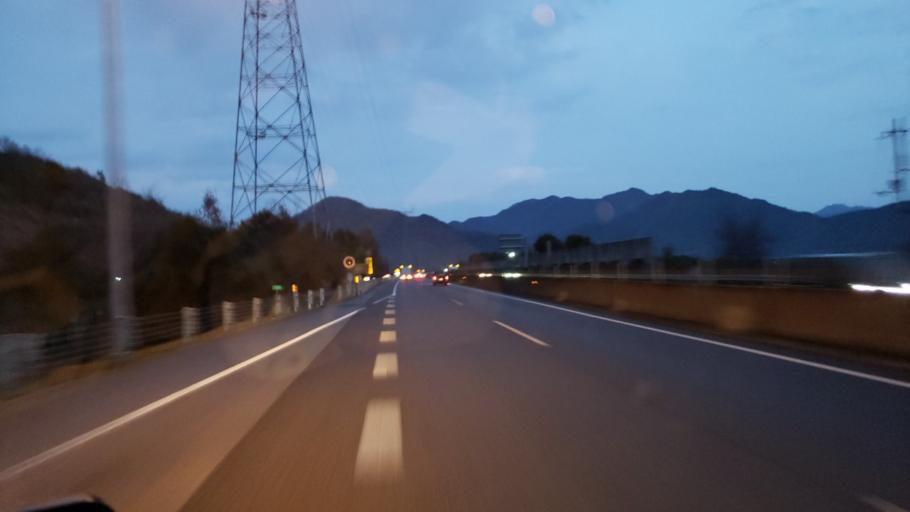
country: JP
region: Hyogo
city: Himeji
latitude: 34.8507
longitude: 134.7454
